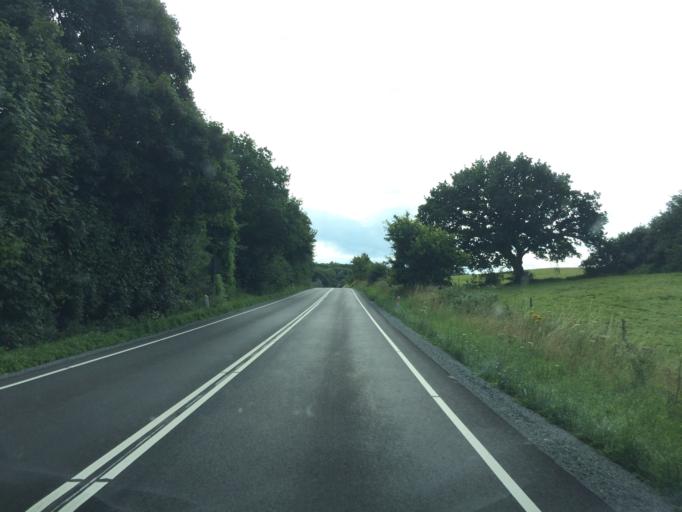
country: DK
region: South Denmark
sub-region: Faaborg-Midtfyn Kommune
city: Faaborg
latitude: 55.1447
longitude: 10.2635
